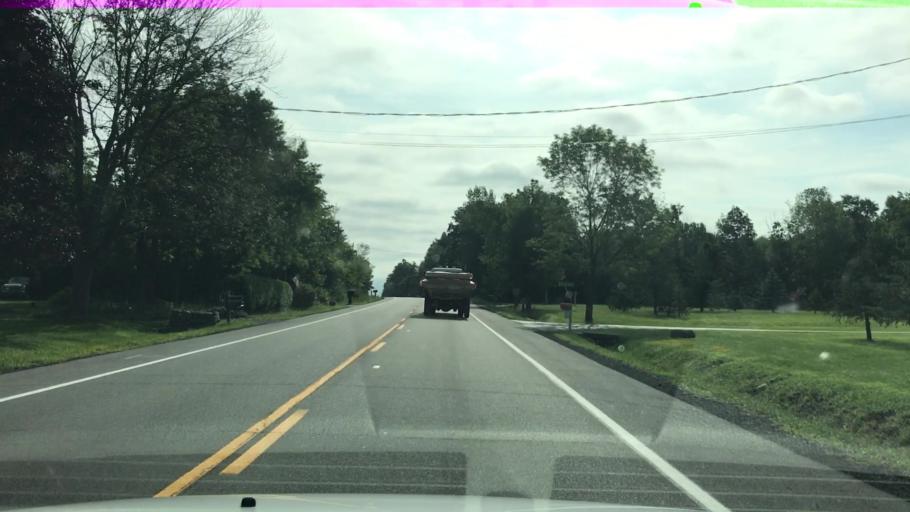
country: US
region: New York
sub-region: Erie County
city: Town Line
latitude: 42.8571
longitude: -78.5486
